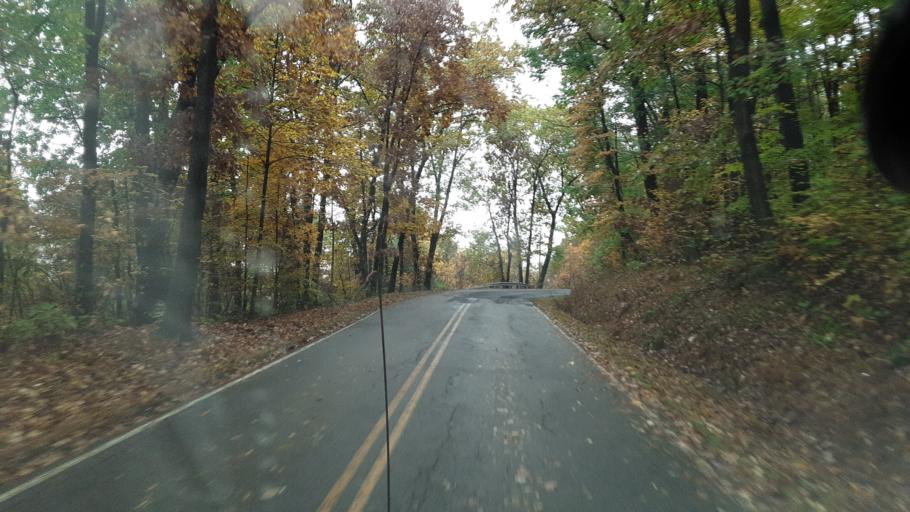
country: US
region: Ohio
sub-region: Coshocton County
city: West Lafayette
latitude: 40.3254
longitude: -81.7886
